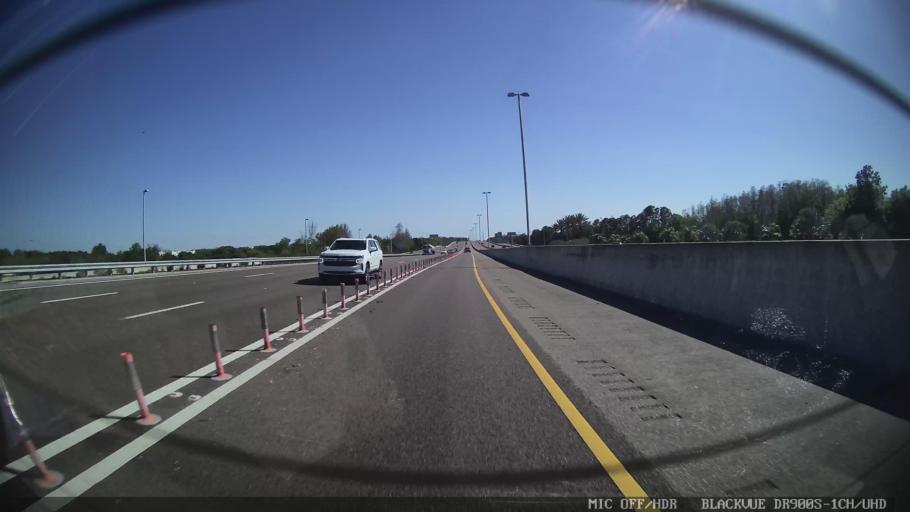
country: US
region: Florida
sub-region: Hillsborough County
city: Town 'n' Country
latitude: 28.0318
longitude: -82.5453
